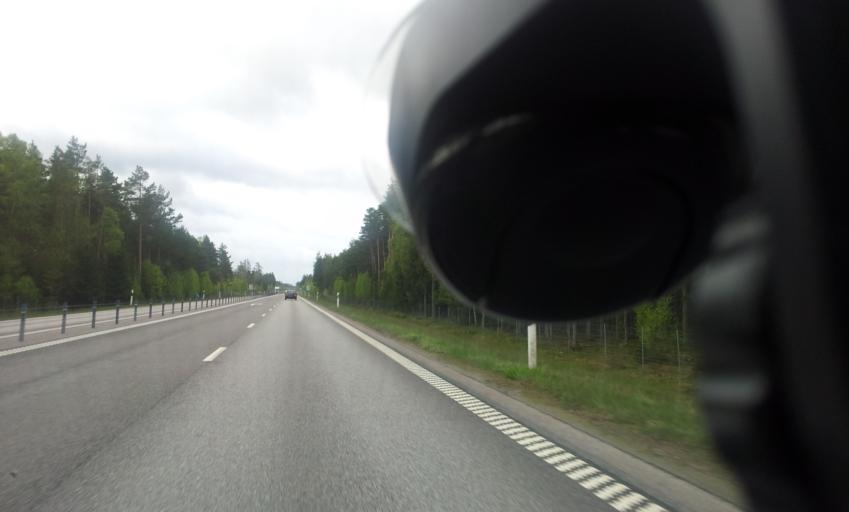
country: SE
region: Kalmar
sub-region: Kalmar Kommun
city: Ljungbyholm
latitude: 56.5326
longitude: 16.0841
